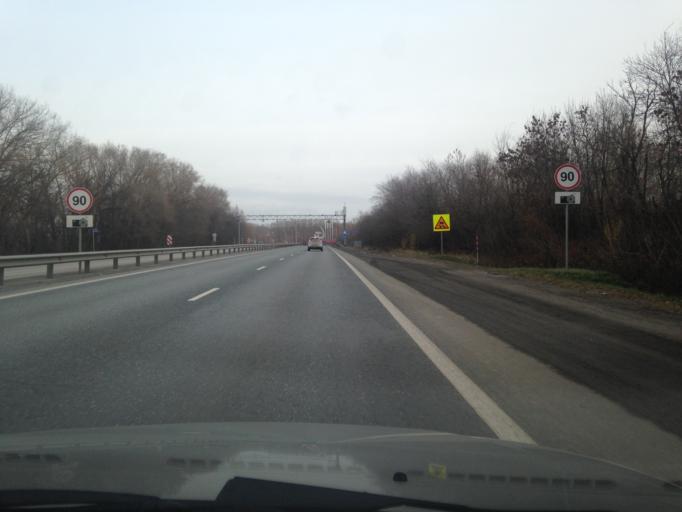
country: RU
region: Ulyanovsk
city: Novoul'yanovsk
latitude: 54.2044
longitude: 48.2922
